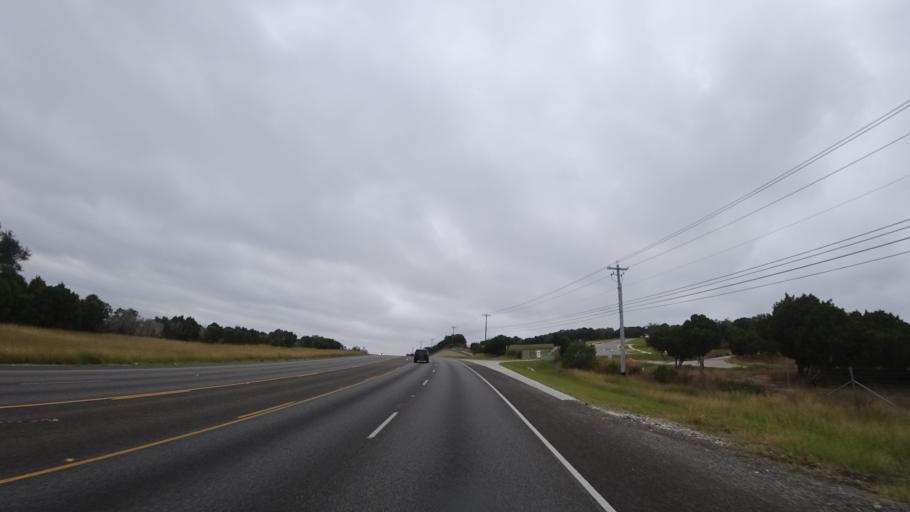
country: US
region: Texas
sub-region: Travis County
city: Bee Cave
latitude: 30.2809
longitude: -97.9169
